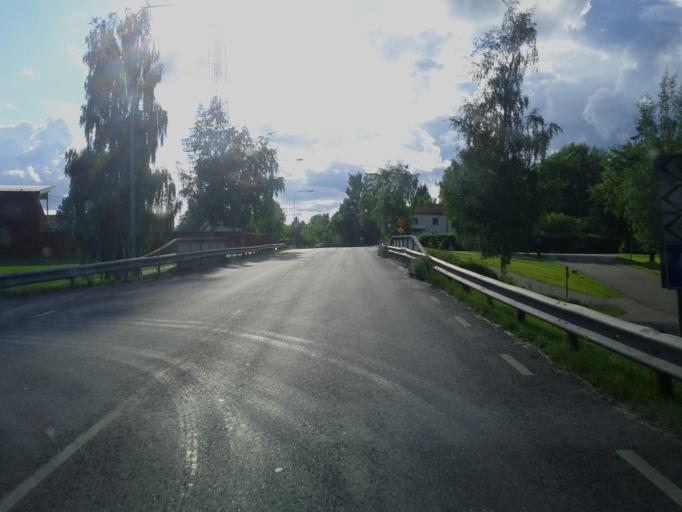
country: SE
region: Dalarna
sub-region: Borlange Kommun
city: Borlaenge
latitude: 60.4953
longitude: 15.4373
